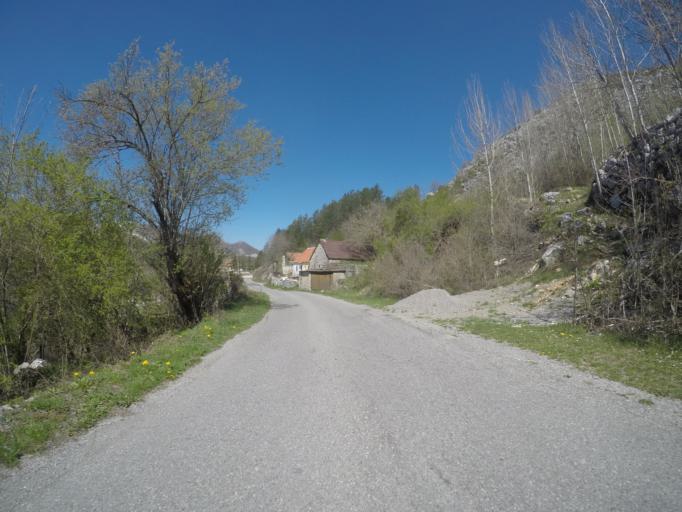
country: ME
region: Cetinje
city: Cetinje
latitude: 42.4634
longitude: 18.8628
